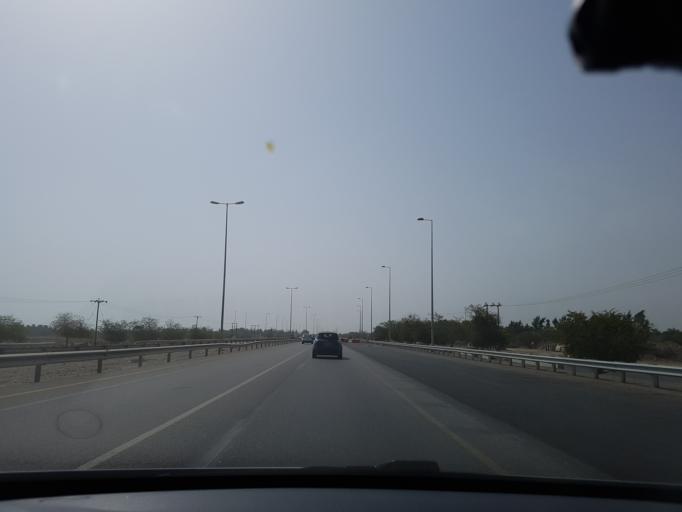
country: OM
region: Al Batinah
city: Al Khaburah
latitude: 23.9991
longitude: 57.0602
